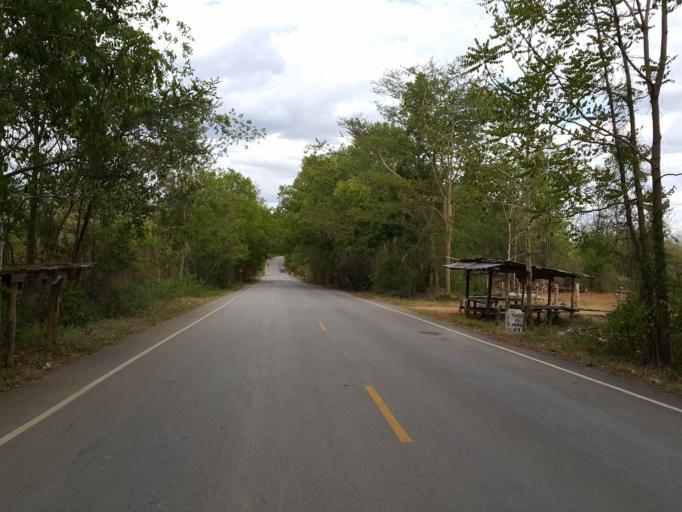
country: TH
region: Sukhothai
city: Thung Saliam
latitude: 17.3502
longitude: 99.4303
